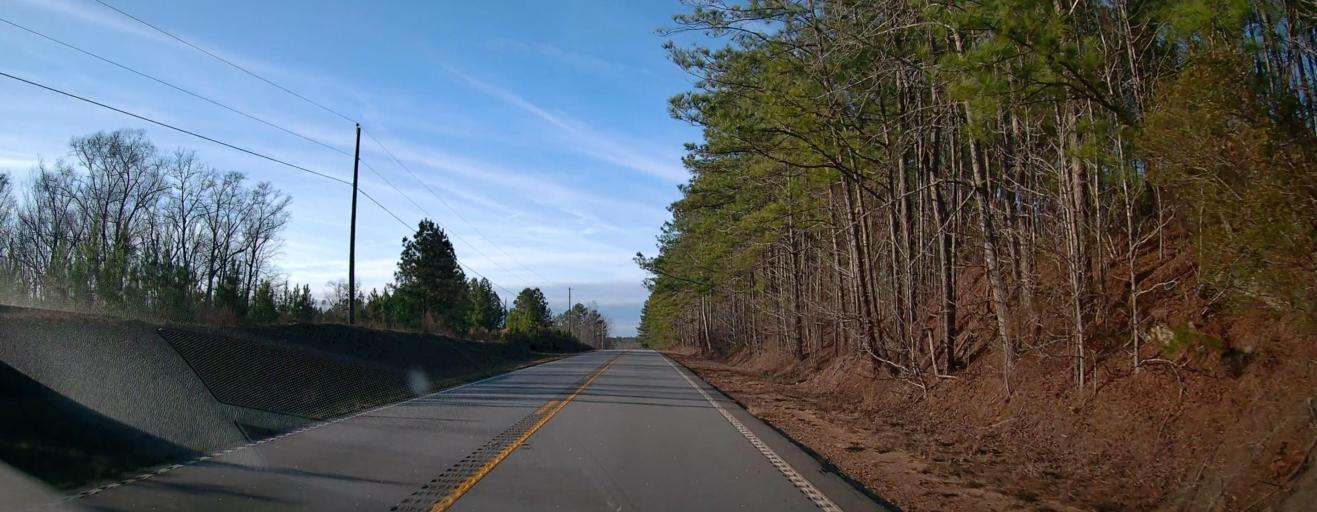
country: US
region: Alabama
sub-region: Chambers County
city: Valley
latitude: 32.7890
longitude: -85.0990
